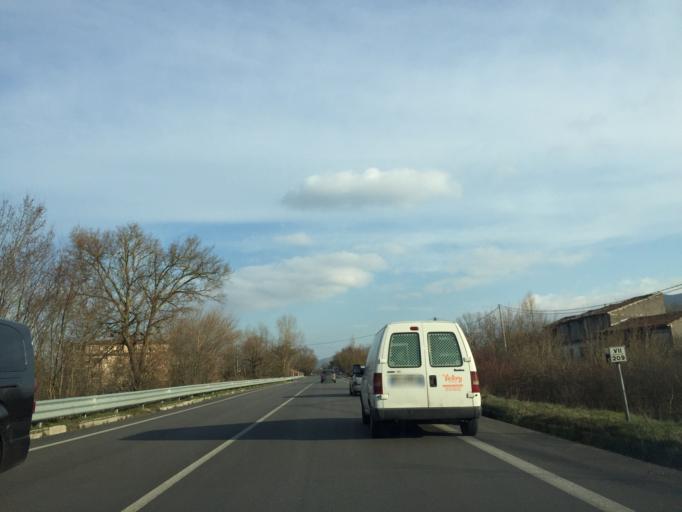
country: IT
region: Molise
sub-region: Provincia di Campobasso
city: San Polomatese
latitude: 41.4783
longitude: 14.5033
